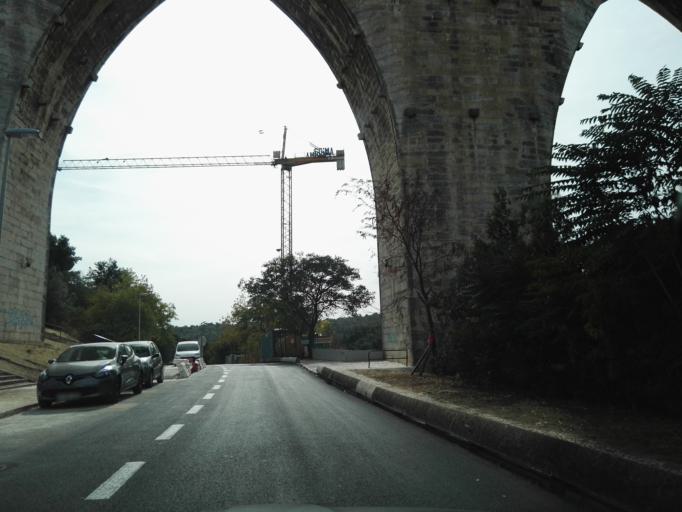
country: PT
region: Lisbon
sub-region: Lisbon
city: Lisbon
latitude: 38.7288
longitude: -9.1687
